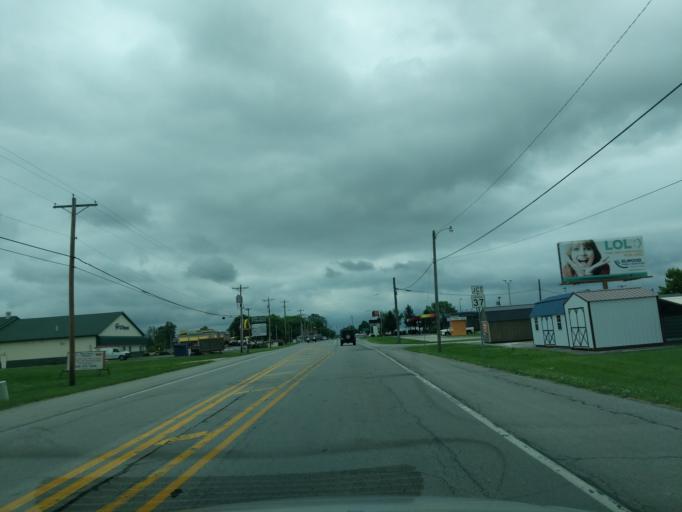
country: US
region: Indiana
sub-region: Madison County
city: Elwood
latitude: 40.2771
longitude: -85.8128
